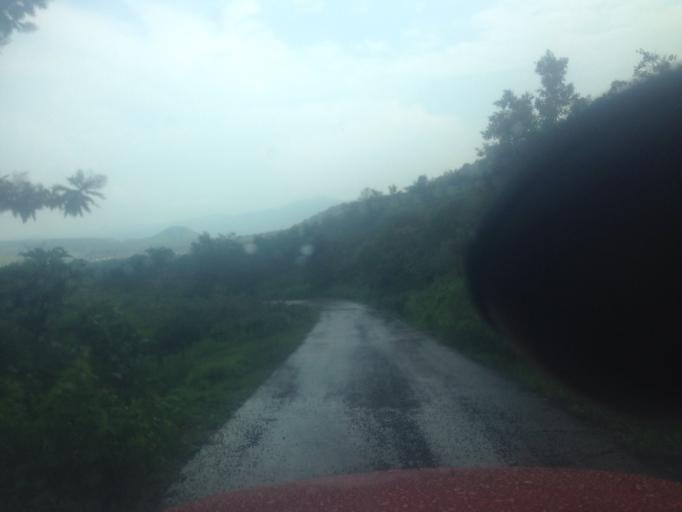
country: MX
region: Nayarit
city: Jala
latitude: 21.1151
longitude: -104.4607
